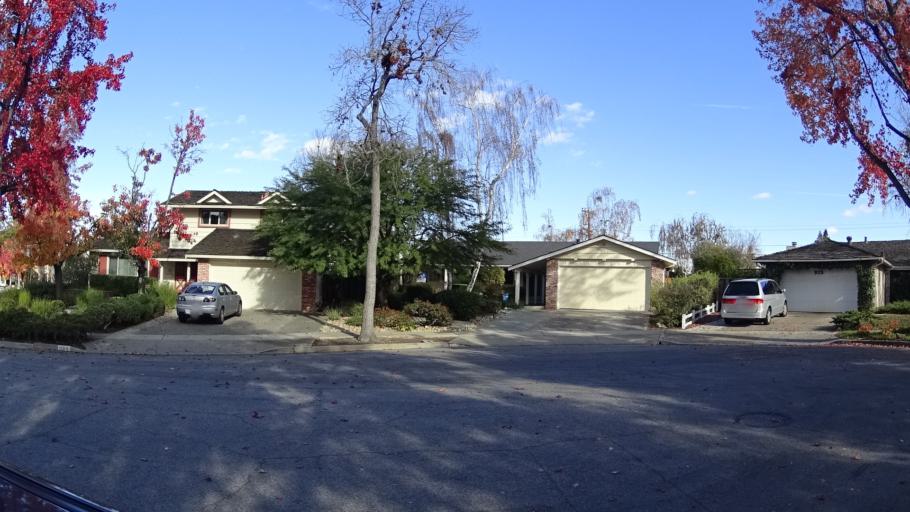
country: US
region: California
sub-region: Santa Clara County
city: Cupertino
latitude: 37.3382
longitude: -122.0522
